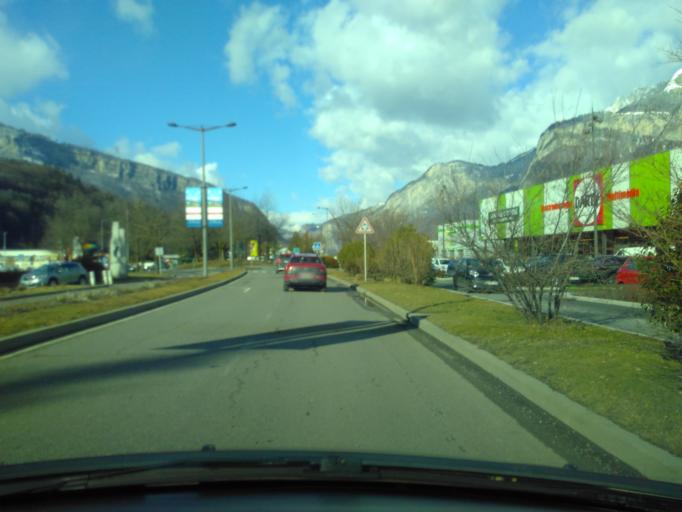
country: FR
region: Rhone-Alpes
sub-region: Departement de la Haute-Savoie
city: Sallanches
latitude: 45.9512
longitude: 6.6300
